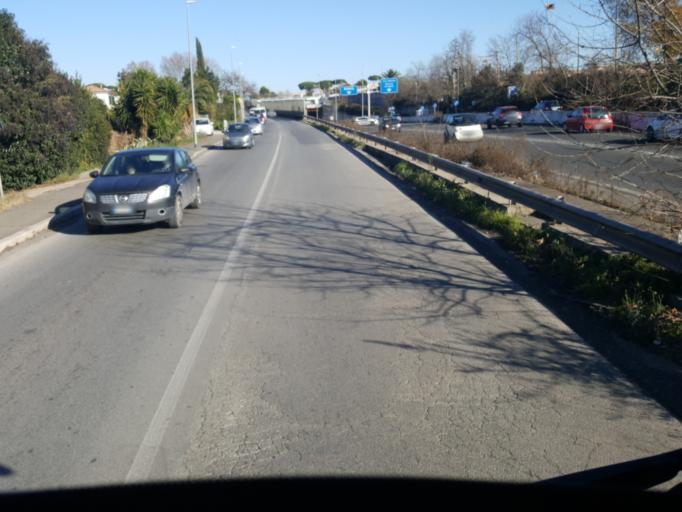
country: IT
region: Latium
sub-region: Citta metropolitana di Roma Capitale
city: Acilia-Castel Fusano-Ostia Antica
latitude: 41.7798
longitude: 12.3511
